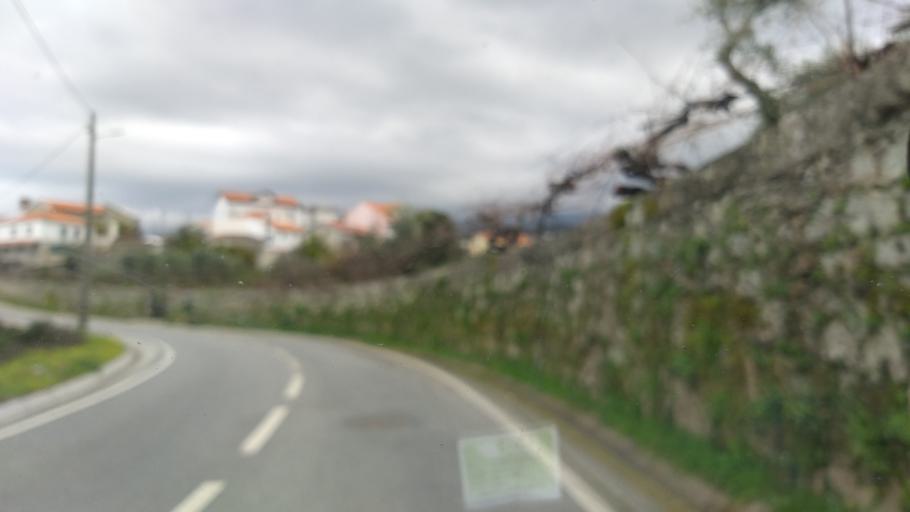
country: PT
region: Guarda
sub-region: Seia
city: Seia
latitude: 40.4729
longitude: -7.6357
